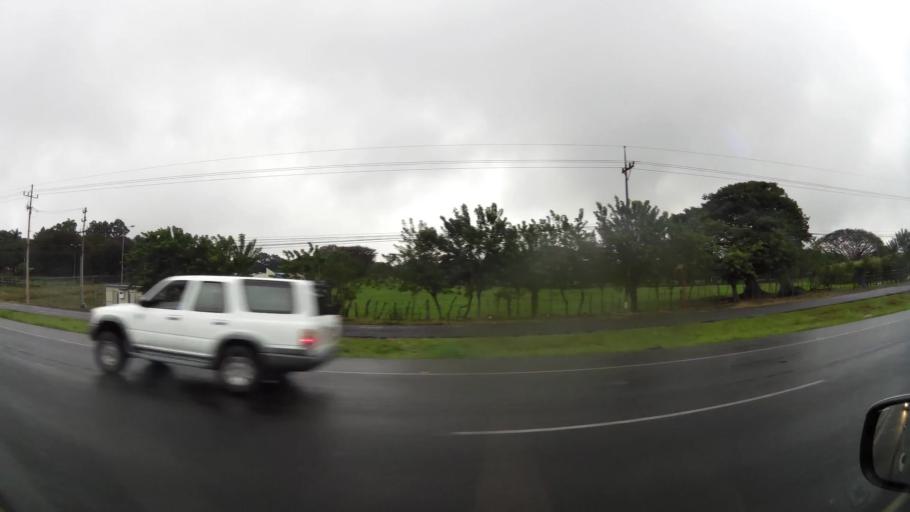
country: CR
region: Alajuela
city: Alajuela
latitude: 9.9945
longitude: -84.2360
